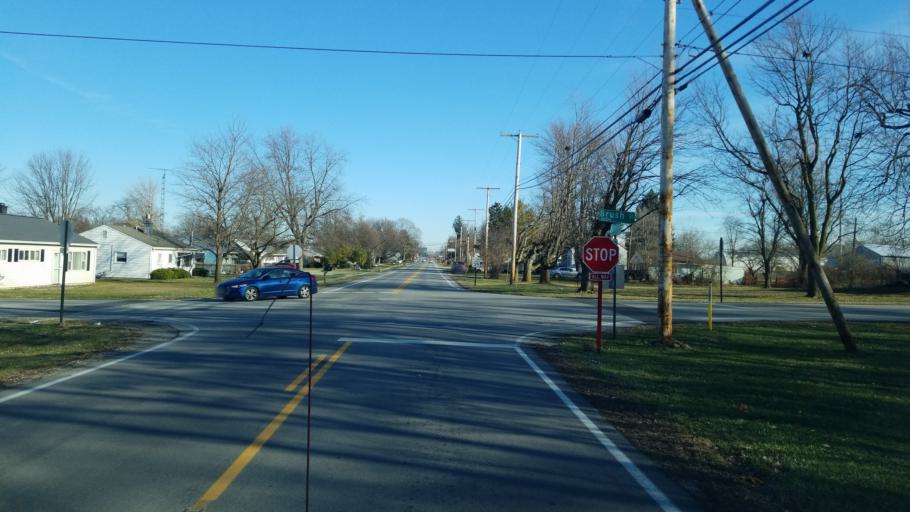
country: US
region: Ohio
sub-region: Sandusky County
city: Stony Prairie
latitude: 41.3494
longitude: -83.1466
